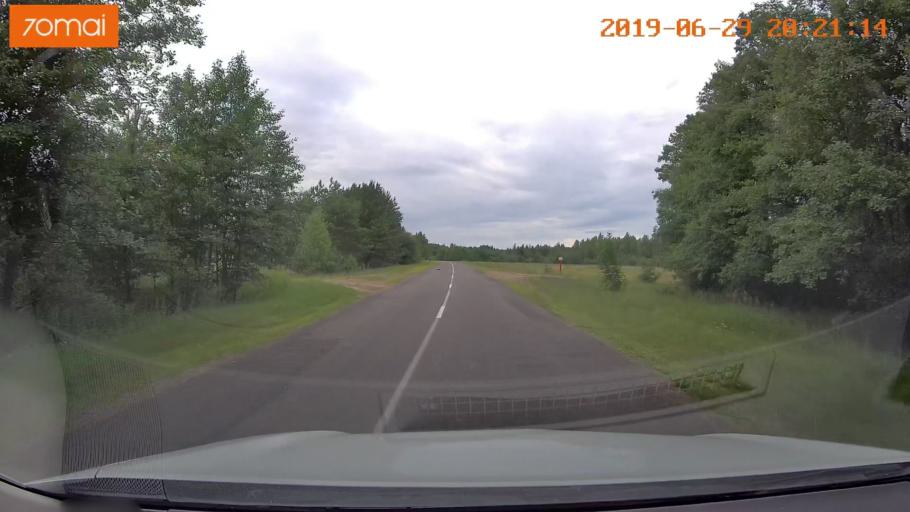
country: BY
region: Brest
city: Asnyezhytsy
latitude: 52.4175
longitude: 26.2526
